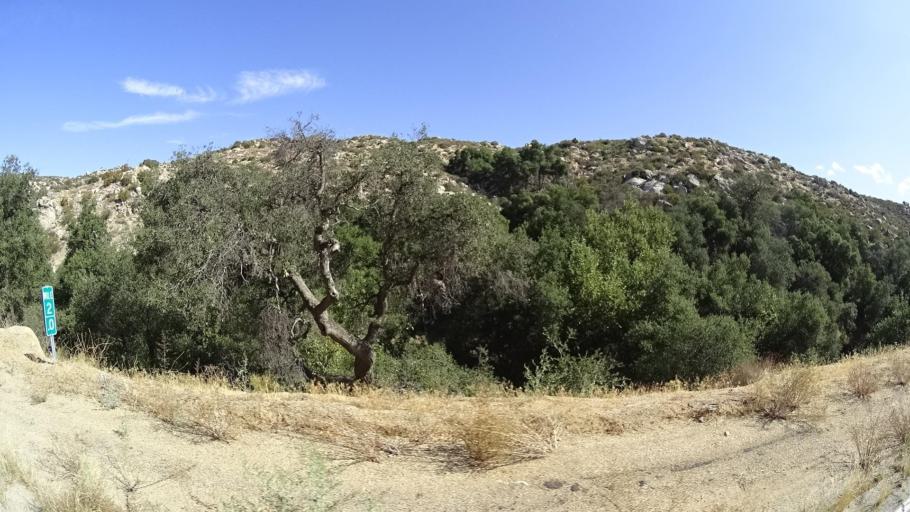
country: US
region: California
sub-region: Riverside County
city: Aguanga
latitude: 33.3738
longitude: -116.7154
